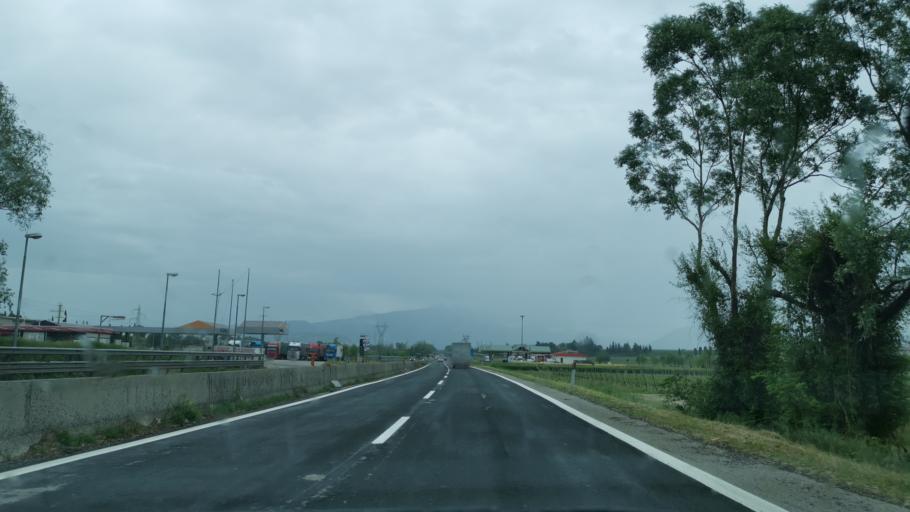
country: IT
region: Veneto
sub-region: Provincia di Verona
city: Cola
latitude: 45.4766
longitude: 10.7636
